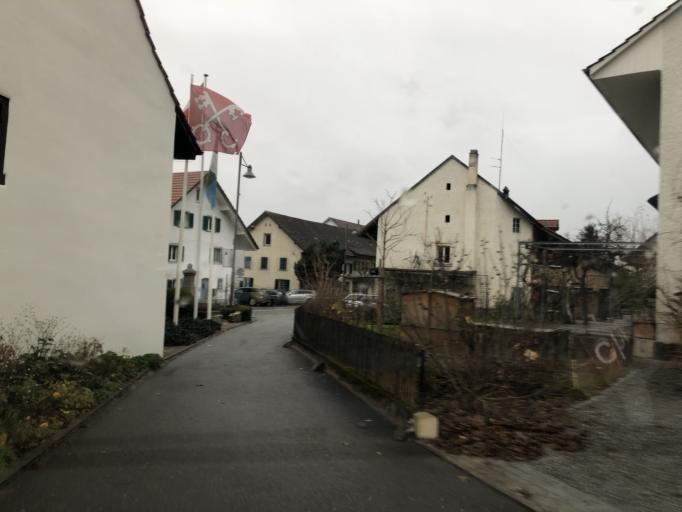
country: CH
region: Aargau
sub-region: Bezirk Baden
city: Untersiggenthal
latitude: 47.4996
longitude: 8.2643
